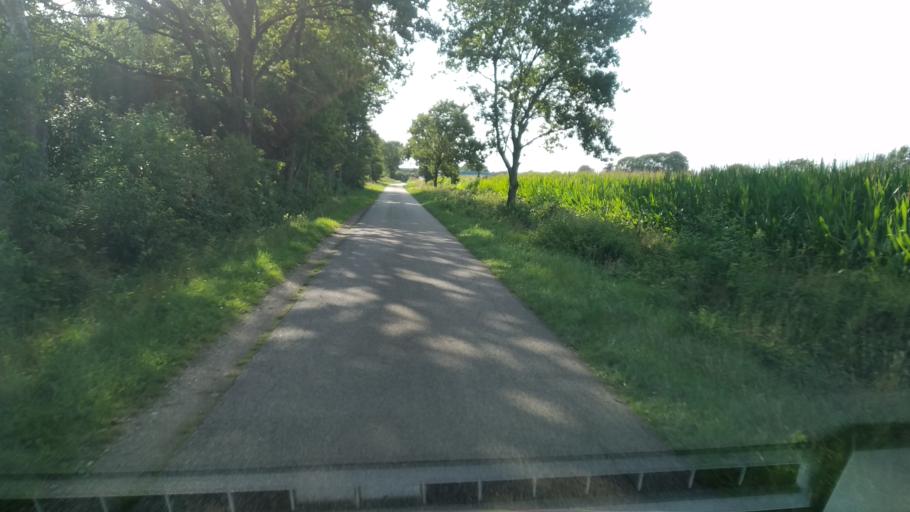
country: DE
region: Schleswig-Holstein
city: Gross Rheide
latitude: 54.4291
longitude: 9.4190
